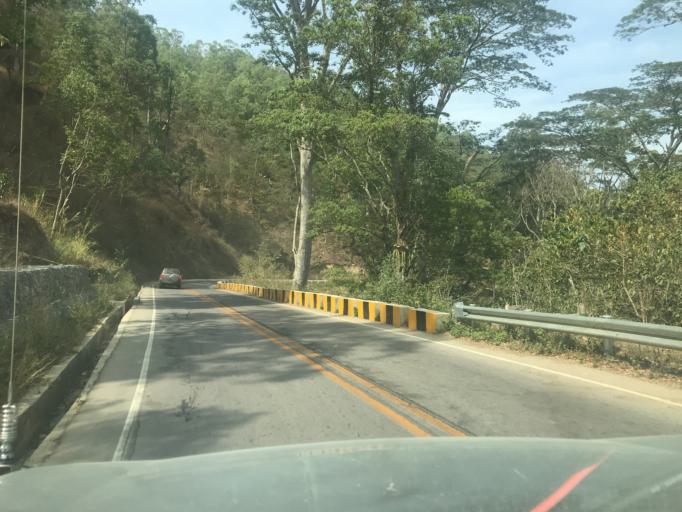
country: TL
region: Aileu
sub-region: Aileu Villa
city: Aileu
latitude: -8.6730
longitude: 125.5553
